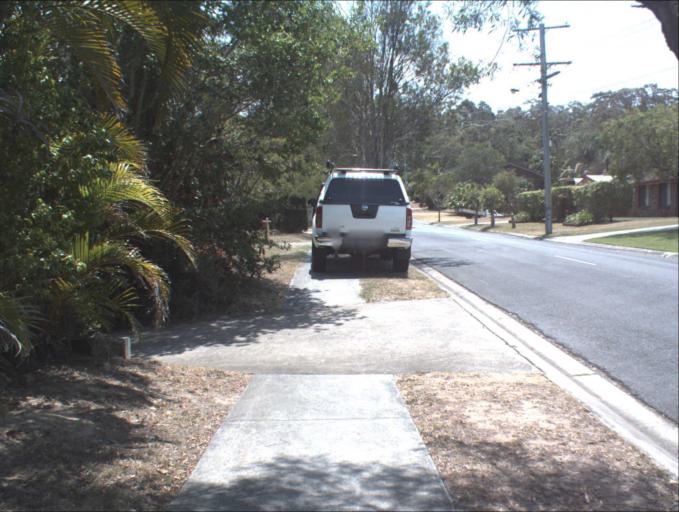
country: AU
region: Queensland
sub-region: Logan
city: Beenleigh
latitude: -27.6674
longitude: 153.1938
